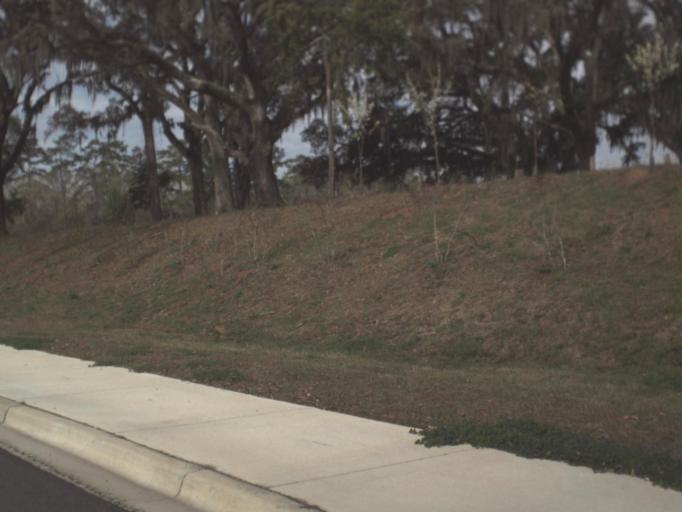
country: US
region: Florida
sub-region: Leon County
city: Tallahassee
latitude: 30.4821
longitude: -84.1672
